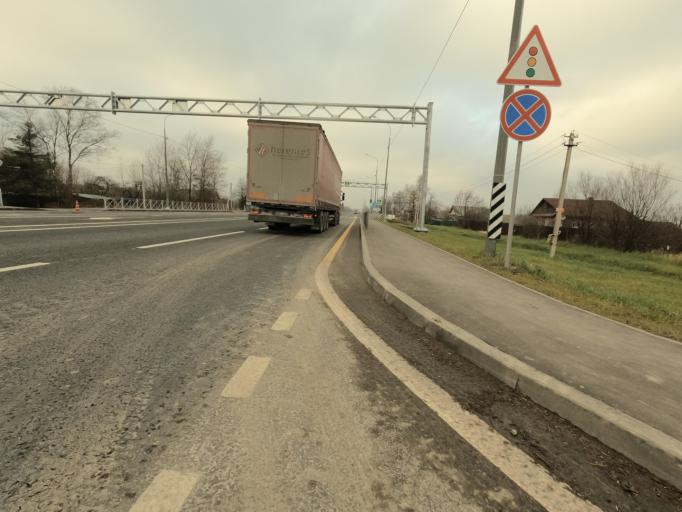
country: RU
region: Leningrad
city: Mga
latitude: 59.7163
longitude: 31.1105
